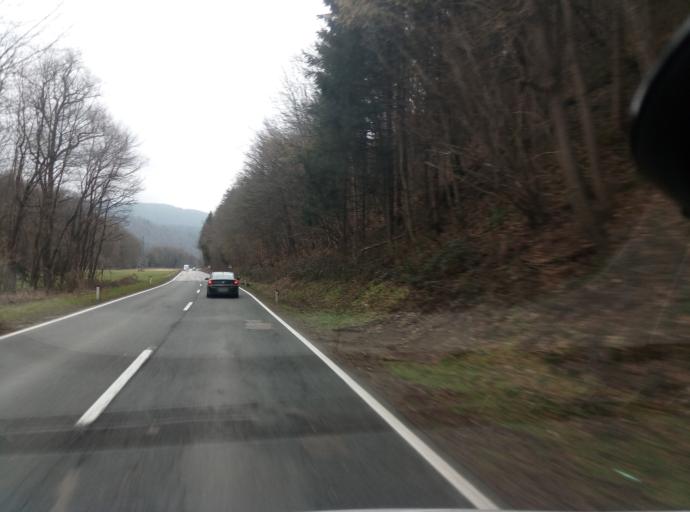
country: SI
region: Smartno pri Litiji
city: Smartno pri Litiji
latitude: 46.0737
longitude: 14.8675
